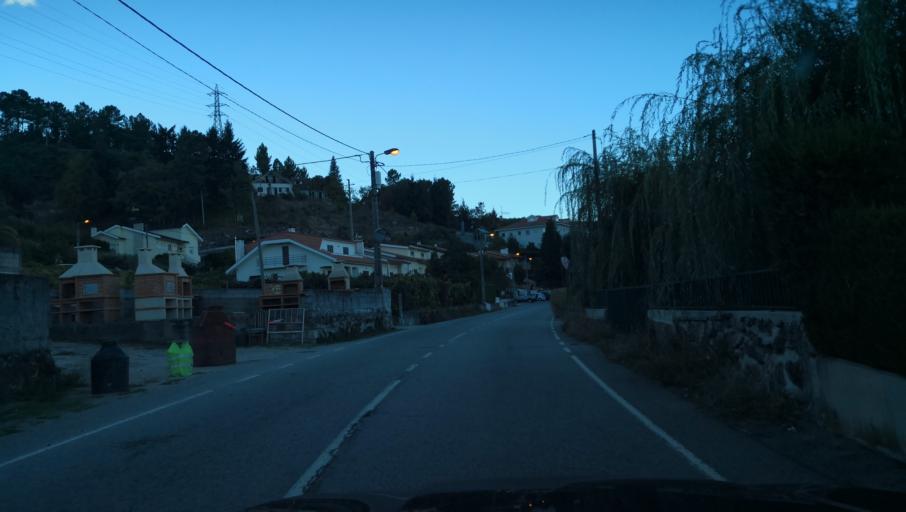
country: PT
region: Vila Real
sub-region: Vila Real
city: Vila Real
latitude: 41.2643
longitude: -7.7745
